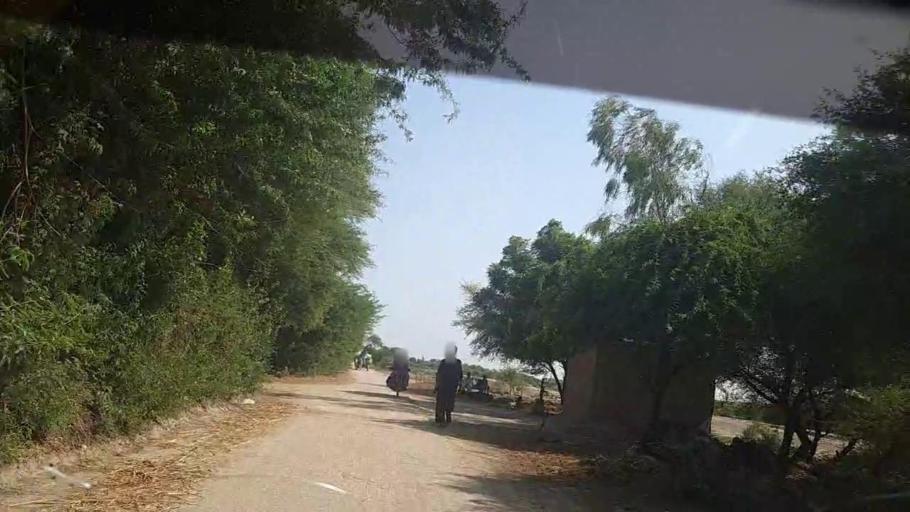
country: PK
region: Sindh
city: Rajo Khanani
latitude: 24.9780
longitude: 68.8668
